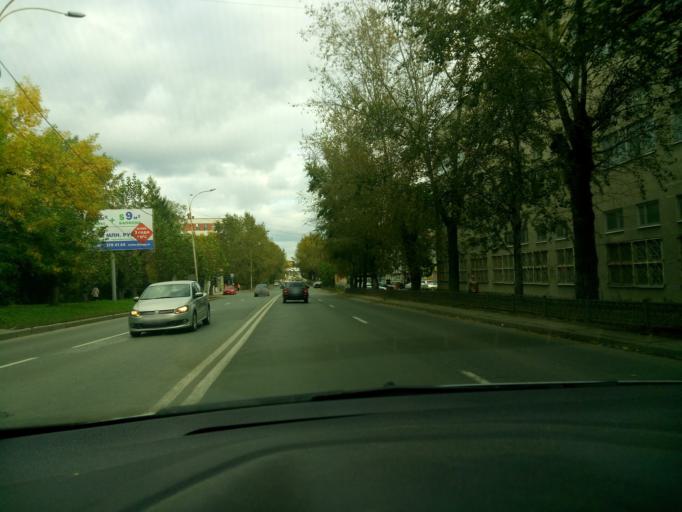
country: RU
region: Sverdlovsk
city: Yekaterinburg
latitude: 56.8255
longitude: 60.6432
